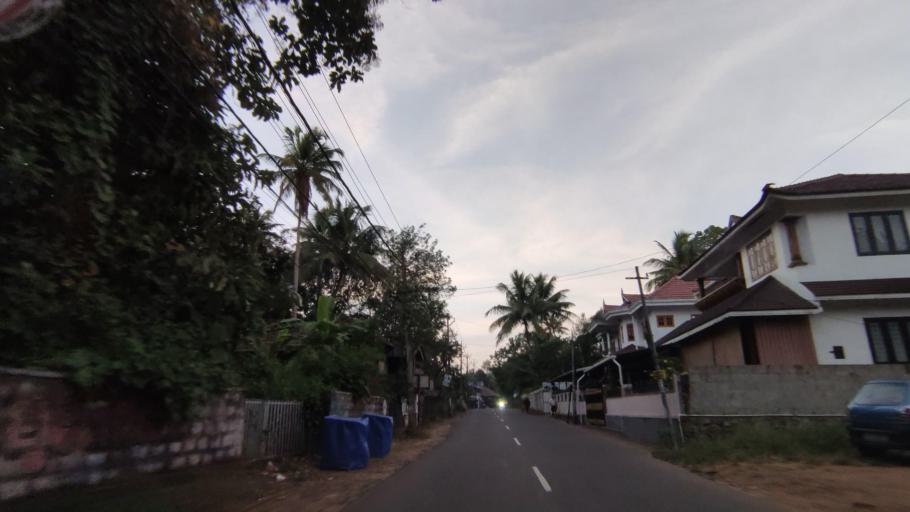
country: IN
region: Kerala
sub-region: Kottayam
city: Kottayam
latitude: 9.6814
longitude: 76.5056
